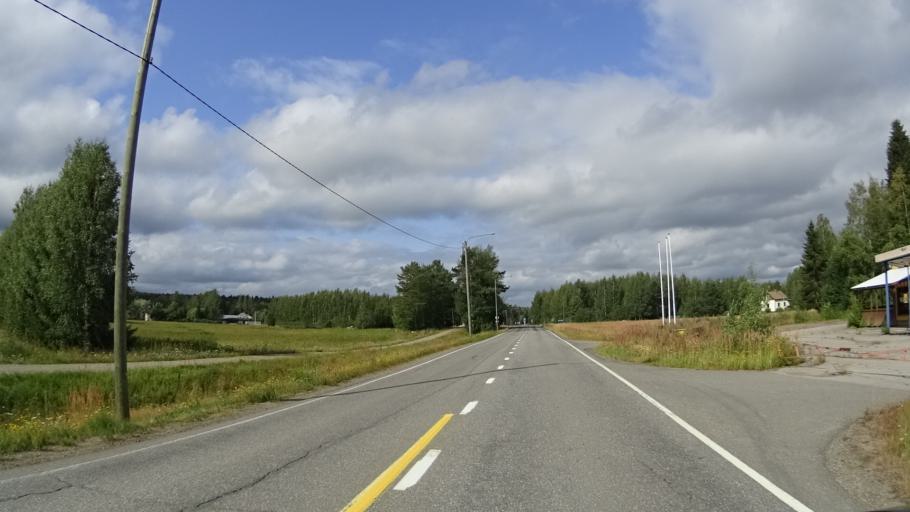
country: FI
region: Pirkanmaa
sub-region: Tampere
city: Luopioinen
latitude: 61.4828
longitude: 24.7098
